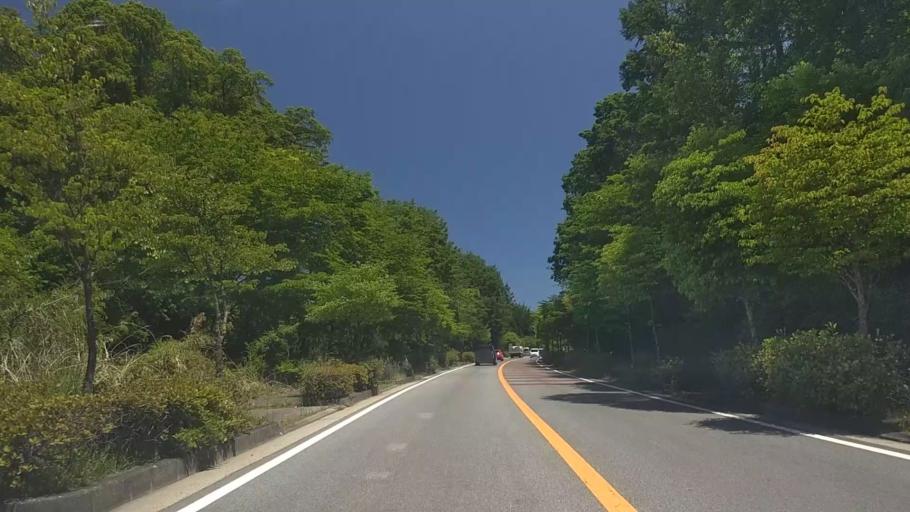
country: JP
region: Yamanashi
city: Nirasaki
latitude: 35.8371
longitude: 138.4305
